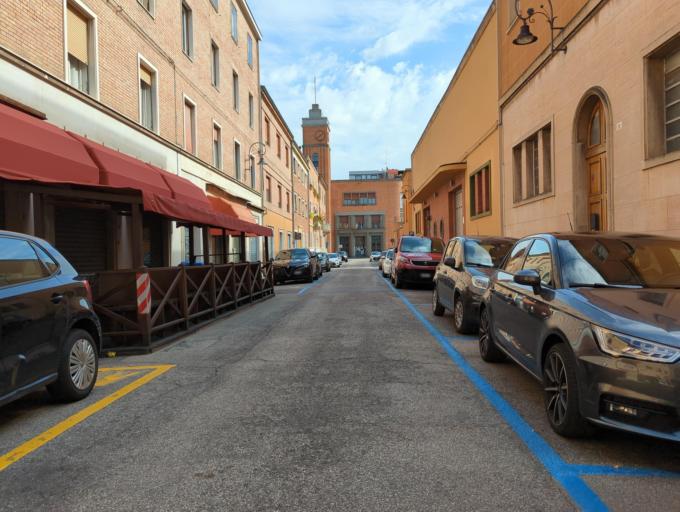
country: IT
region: Emilia-Romagna
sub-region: Provincia di Ferrara
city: Ferrara
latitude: 44.8388
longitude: 11.6211
